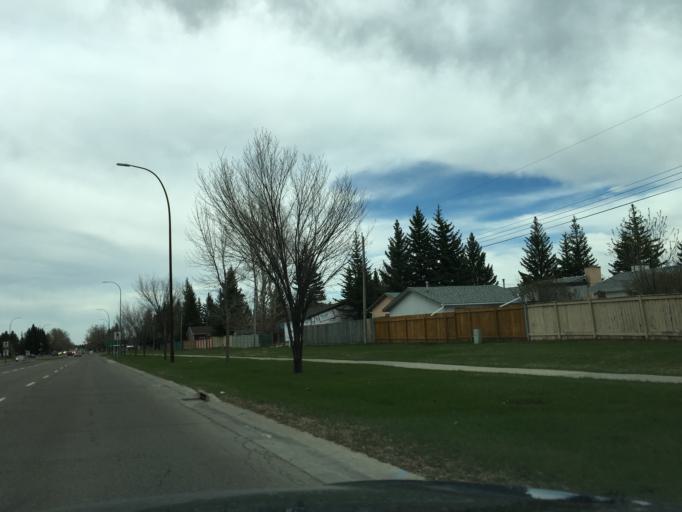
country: CA
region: Alberta
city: Calgary
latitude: 50.9613
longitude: -114.1226
